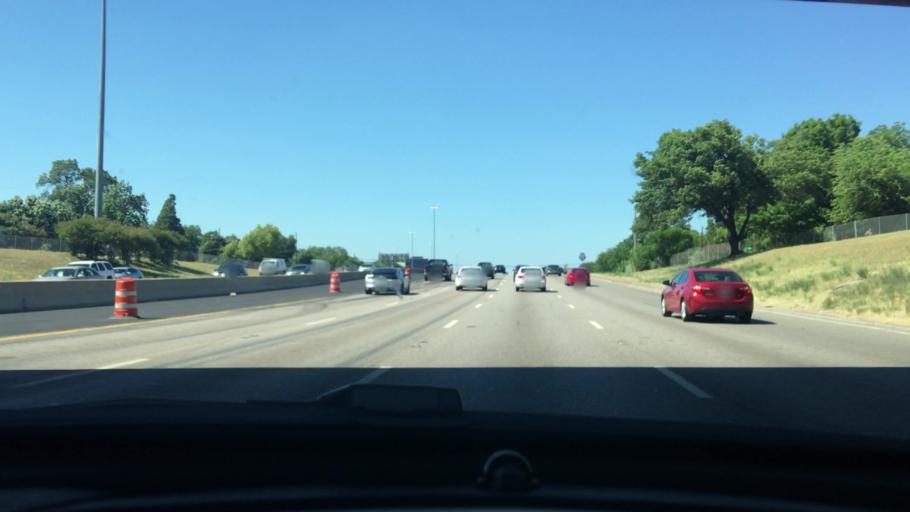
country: US
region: Texas
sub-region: Dallas County
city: Cockrell Hill
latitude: 32.7234
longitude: -96.8266
